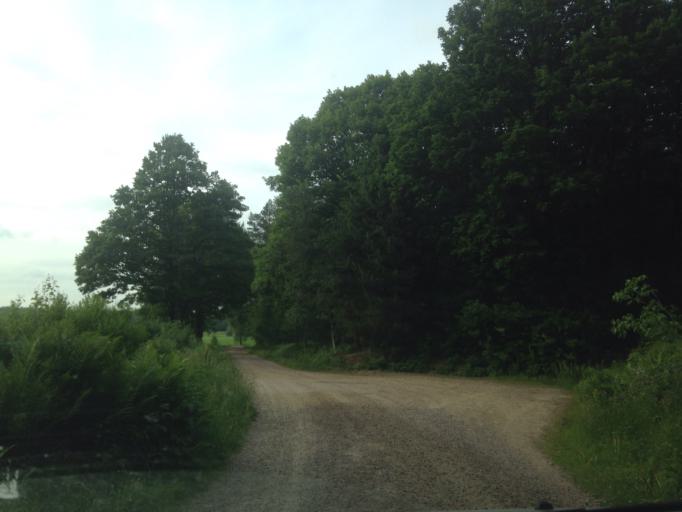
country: SE
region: Vaestra Goetaland
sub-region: Kungalvs Kommun
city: Kungalv
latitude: 57.8142
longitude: 11.9305
